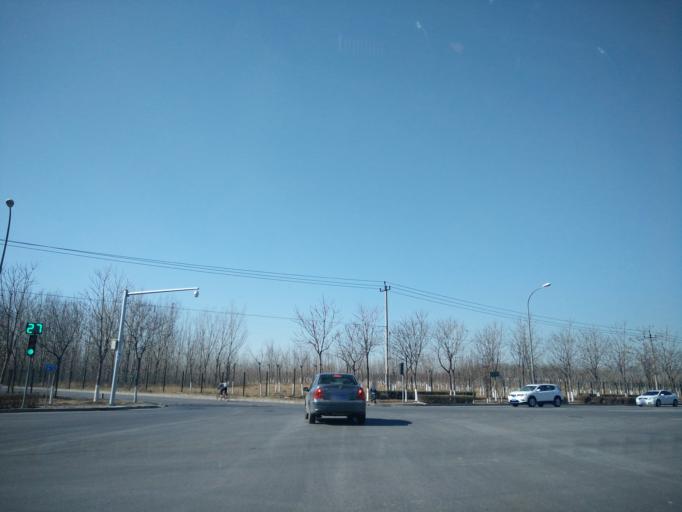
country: CN
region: Beijing
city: Jiugong
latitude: 39.7811
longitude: 116.5434
